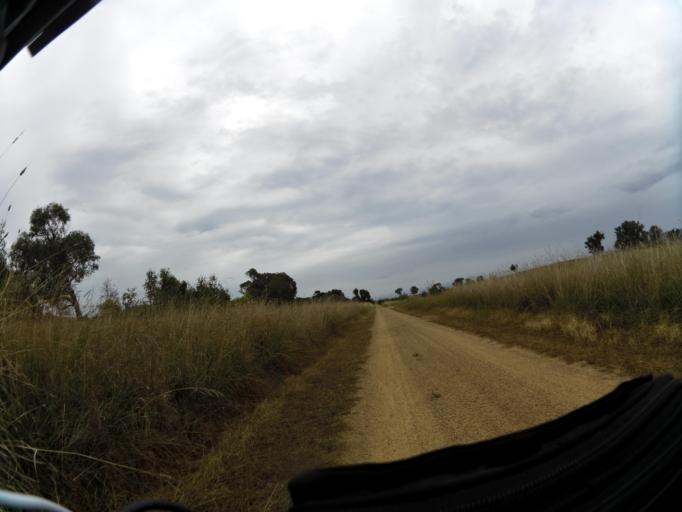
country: AU
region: New South Wales
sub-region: Albury Municipality
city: East Albury
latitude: -36.2084
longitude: 147.0532
